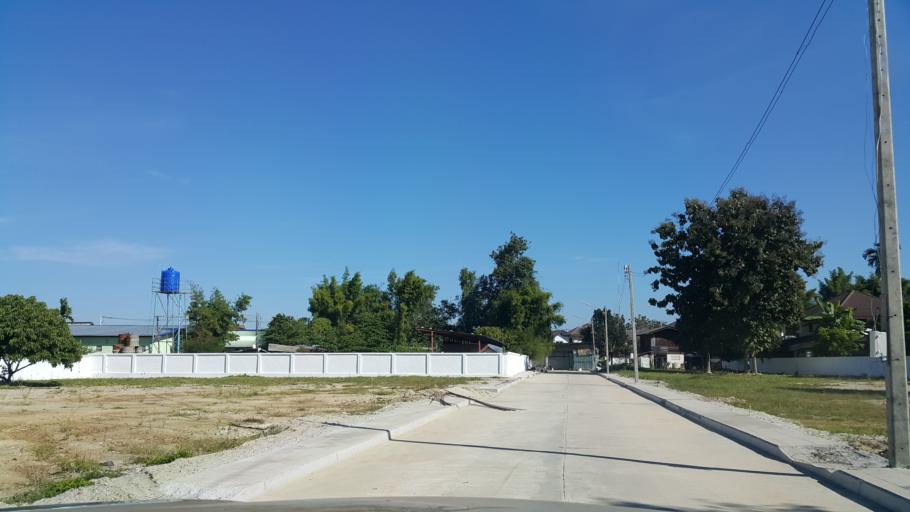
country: TH
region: Chiang Mai
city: San Sai
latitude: 18.8481
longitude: 98.9969
